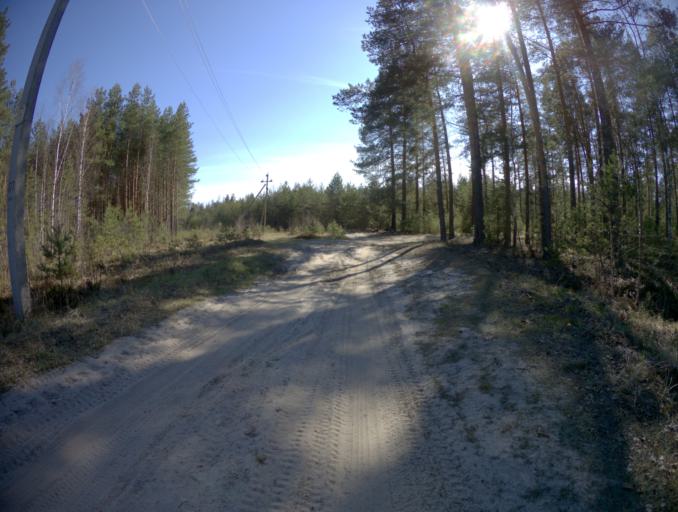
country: RU
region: Vladimir
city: Ivanishchi
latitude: 55.7600
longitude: 40.4069
